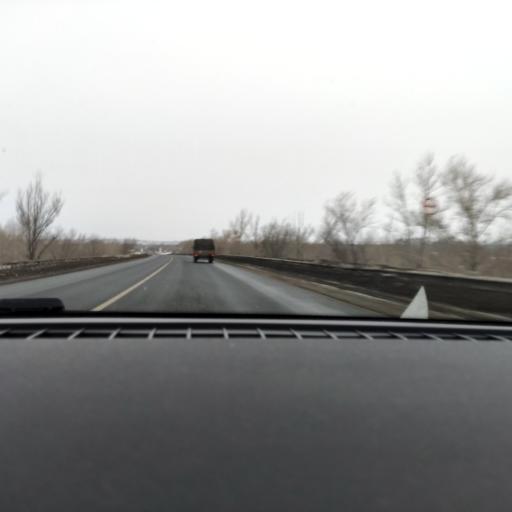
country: RU
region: Samara
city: Kinel'
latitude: 53.1869
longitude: 50.5161
